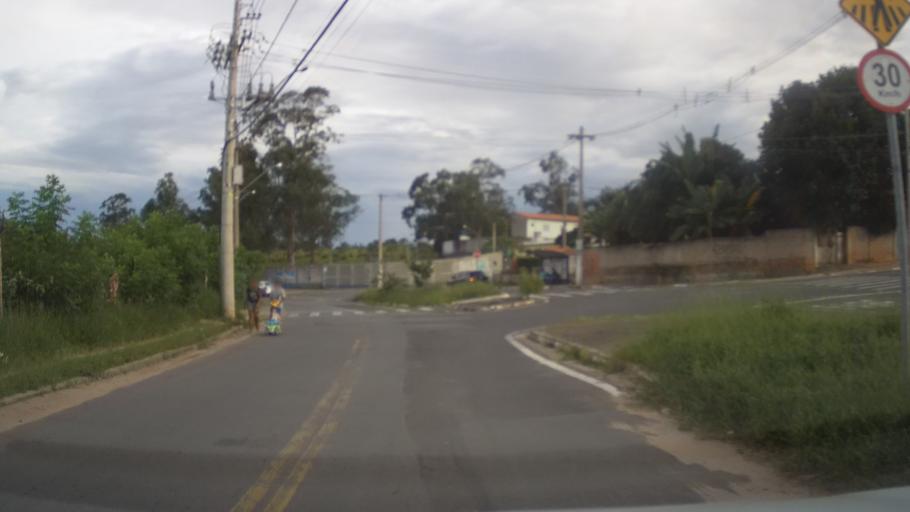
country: BR
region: Sao Paulo
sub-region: Hortolandia
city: Hortolandia
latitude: -22.9562
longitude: -47.2149
